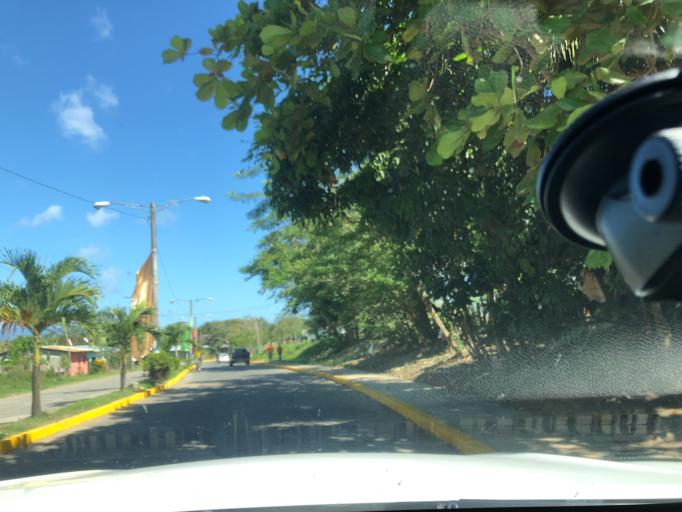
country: NI
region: Rivas
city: Cardenas
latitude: 11.1927
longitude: -85.5127
